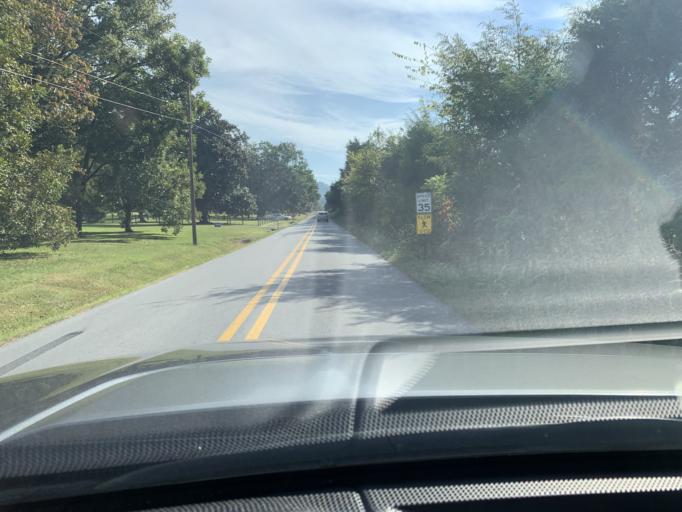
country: US
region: Georgia
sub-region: Polk County
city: Aragon
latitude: 34.0356
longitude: -85.0450
